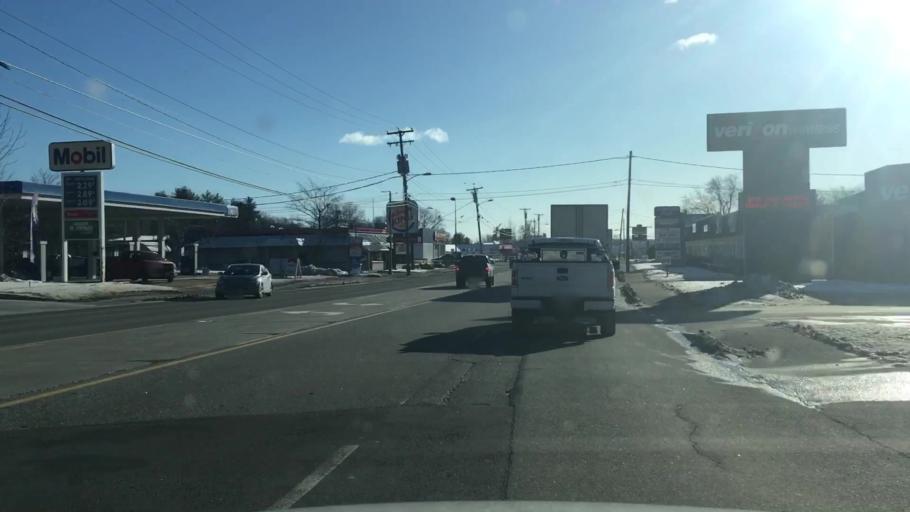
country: US
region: Maine
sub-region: Androscoggin County
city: Lewiston
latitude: 44.1152
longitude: -70.2245
